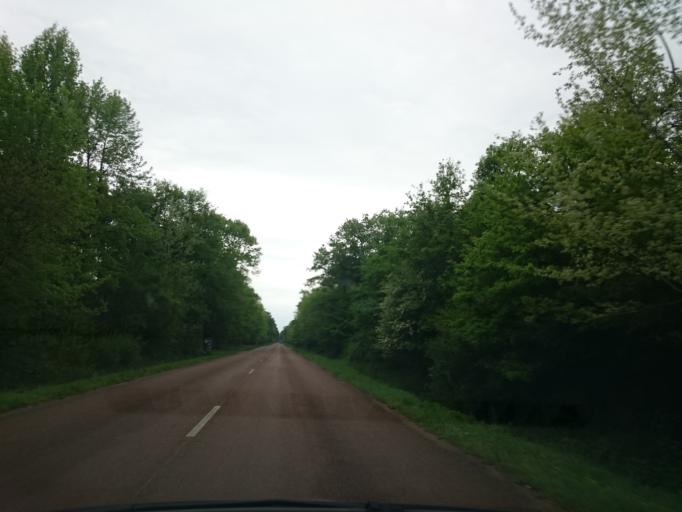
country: FR
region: Centre
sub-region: Departement du Loir-et-Cher
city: Muides-sur-Loire
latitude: 47.6457
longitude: 1.5261
